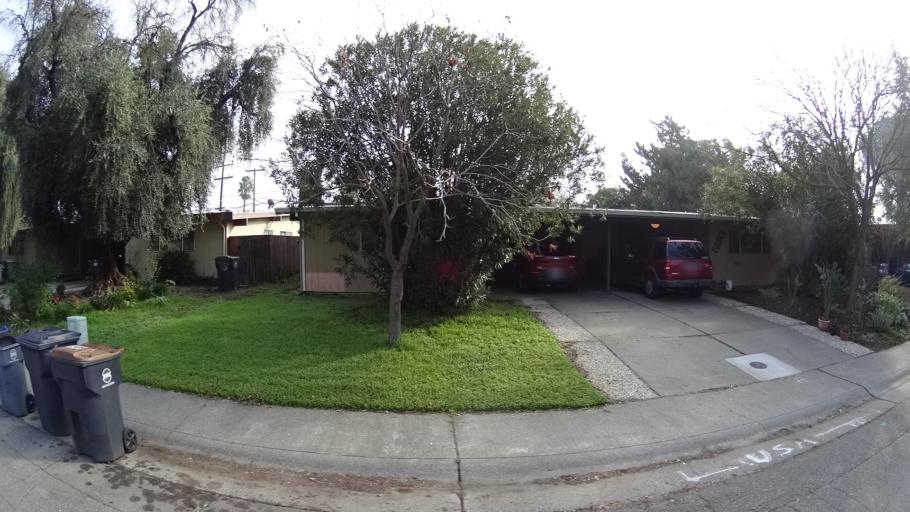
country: US
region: California
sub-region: Yolo County
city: Davis
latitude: 38.5596
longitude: -121.7606
